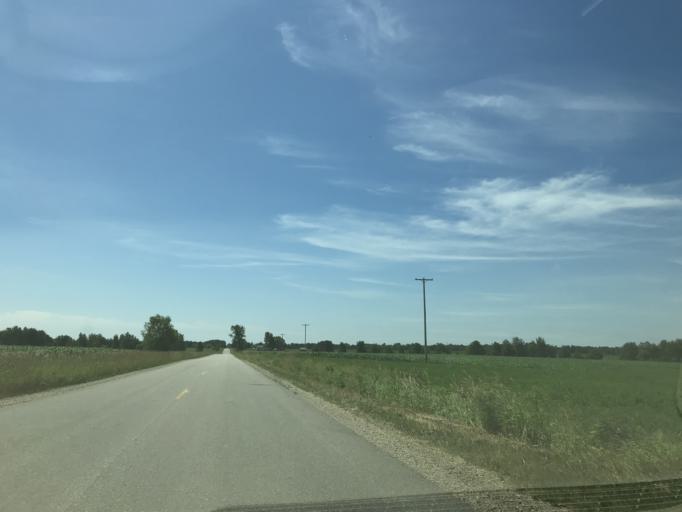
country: US
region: Michigan
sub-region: Missaukee County
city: Lake City
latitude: 44.2841
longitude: -85.0743
